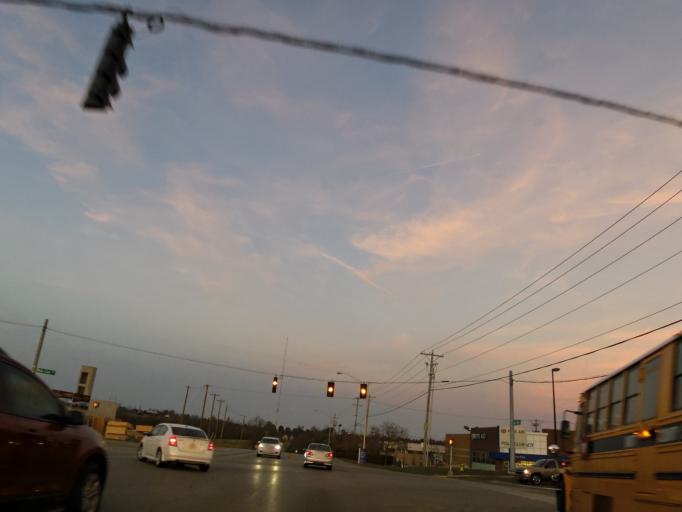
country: US
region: Kentucky
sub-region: Fayette County
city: Lexington-Fayette
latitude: 38.0249
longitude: -84.4066
